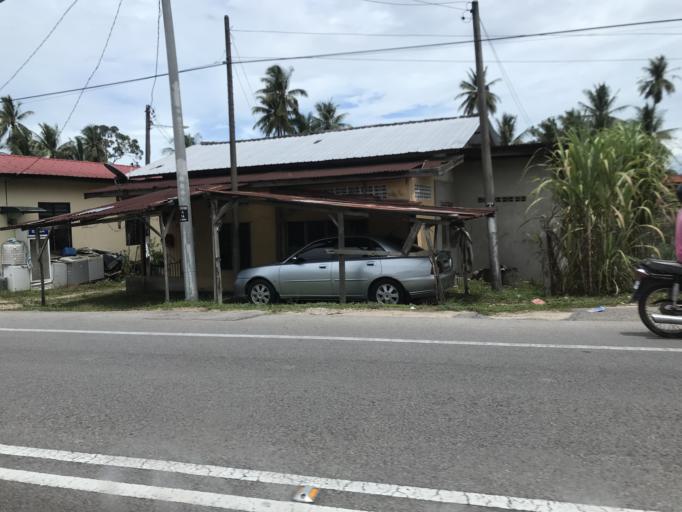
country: MY
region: Kelantan
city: Tumpat
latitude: 6.1721
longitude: 102.1859
